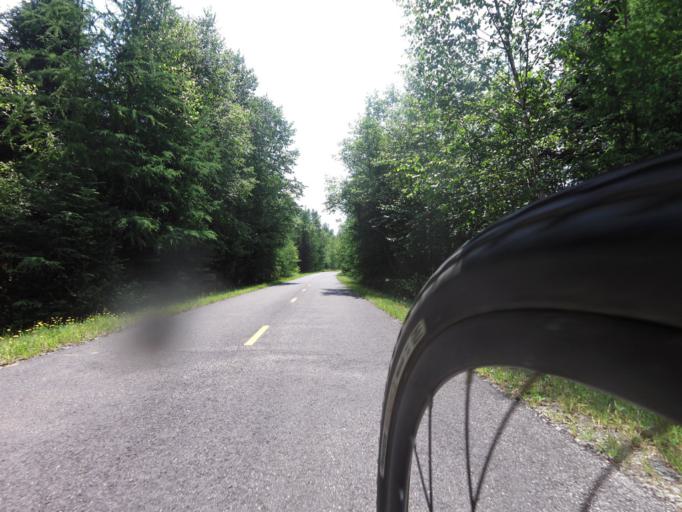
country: CA
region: Quebec
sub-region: Laurentides
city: Mont-Tremblant
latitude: 46.1458
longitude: -74.5935
